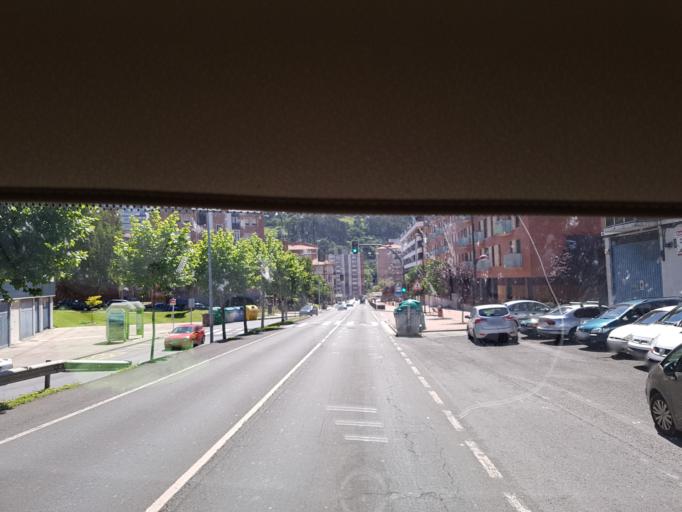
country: ES
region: Basque Country
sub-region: Bizkaia
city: Barakaldo
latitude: 43.2841
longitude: -2.9901
